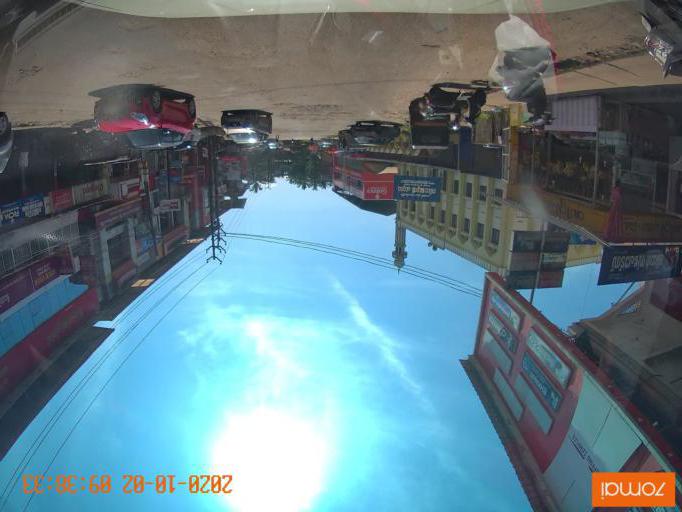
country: IN
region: Kerala
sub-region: Kozhikode
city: Nadapuram
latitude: 11.6543
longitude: 75.7547
